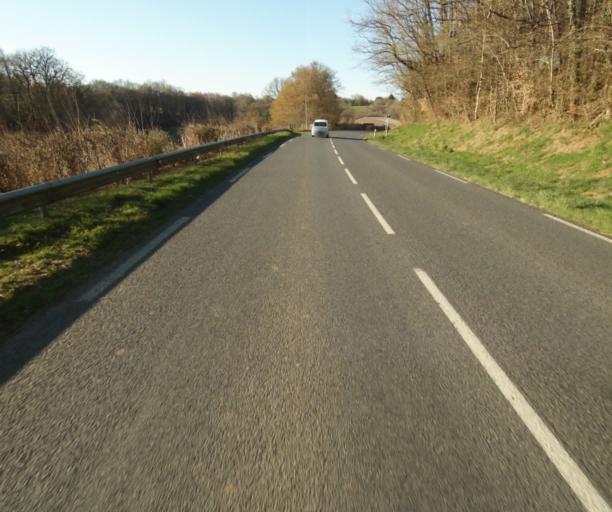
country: FR
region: Limousin
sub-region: Departement de la Correze
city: Seilhac
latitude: 45.3970
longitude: 1.7169
